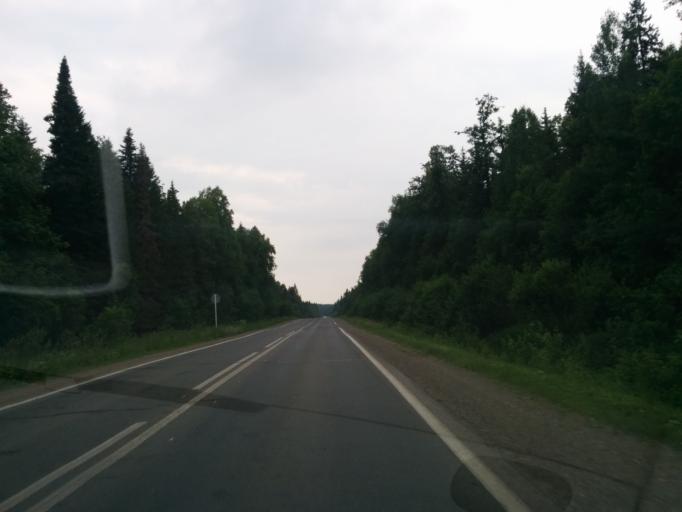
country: RU
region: Perm
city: Perm
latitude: 58.1864
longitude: 56.2194
